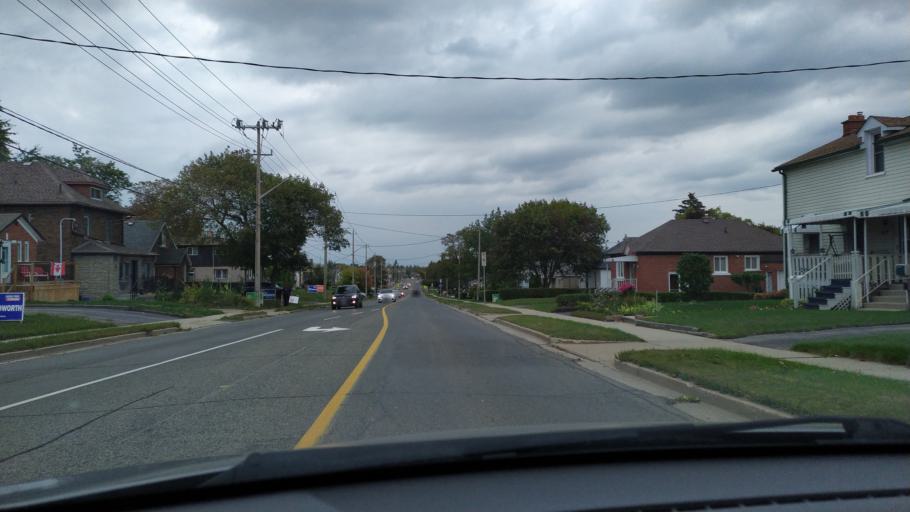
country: CA
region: Ontario
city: Waterloo
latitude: 43.4657
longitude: -80.4842
